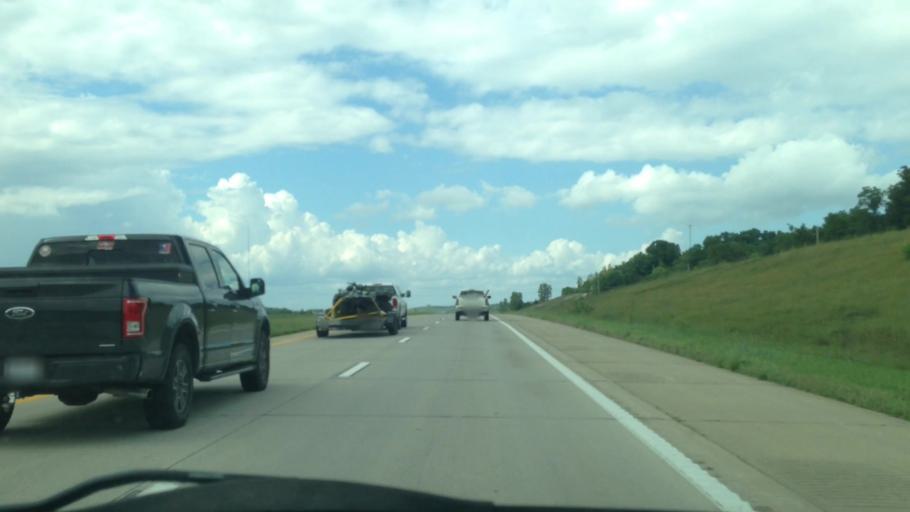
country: US
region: Missouri
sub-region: Pike County
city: Bowling Green
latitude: 39.4336
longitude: -91.2583
